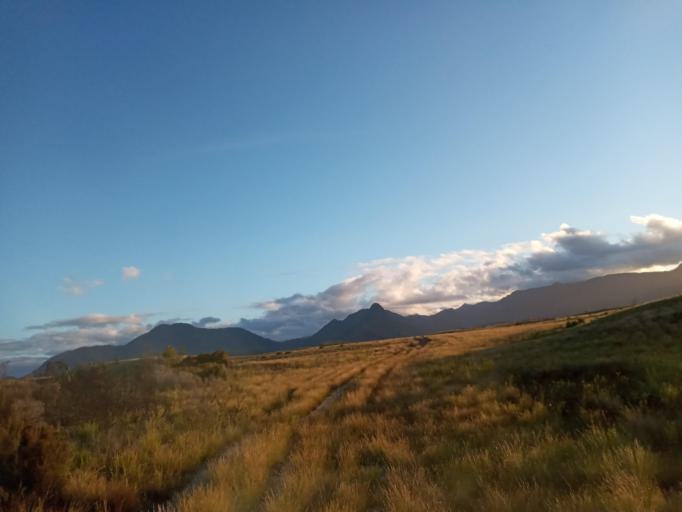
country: MG
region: Anosy
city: Fort Dauphin
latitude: -24.5142
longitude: 47.2486
